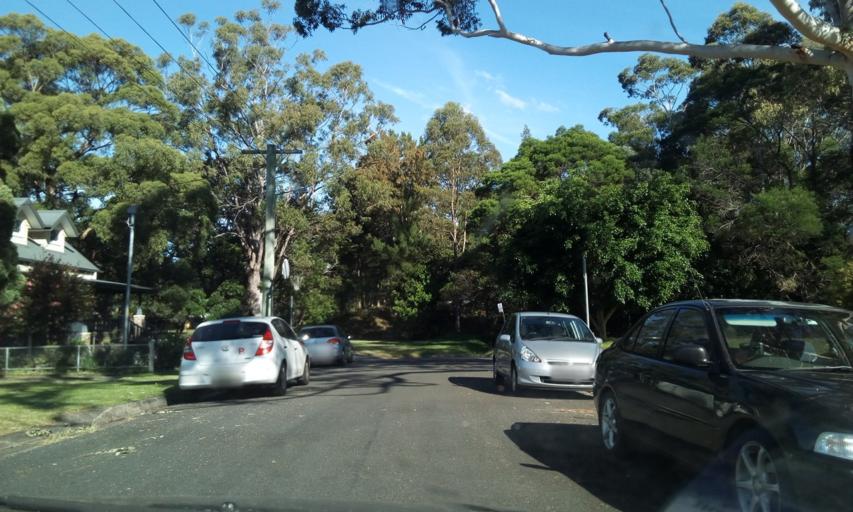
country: AU
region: New South Wales
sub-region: Wollongong
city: Keiraville
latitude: -34.4130
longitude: 150.8739
